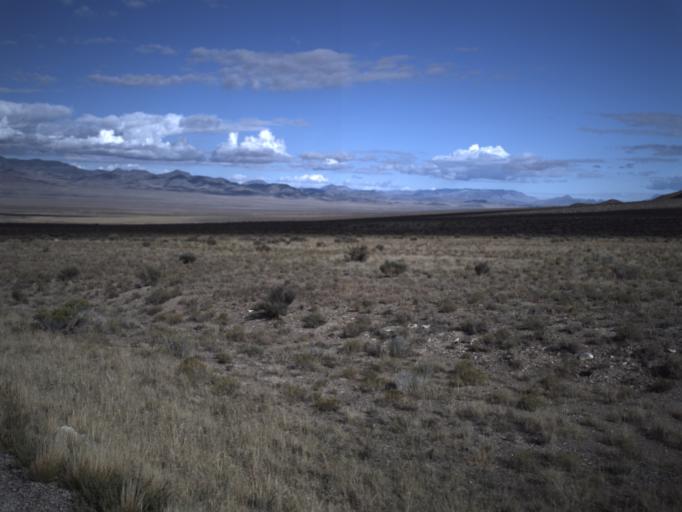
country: US
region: Utah
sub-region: Beaver County
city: Milford
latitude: 38.4411
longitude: -113.3186
